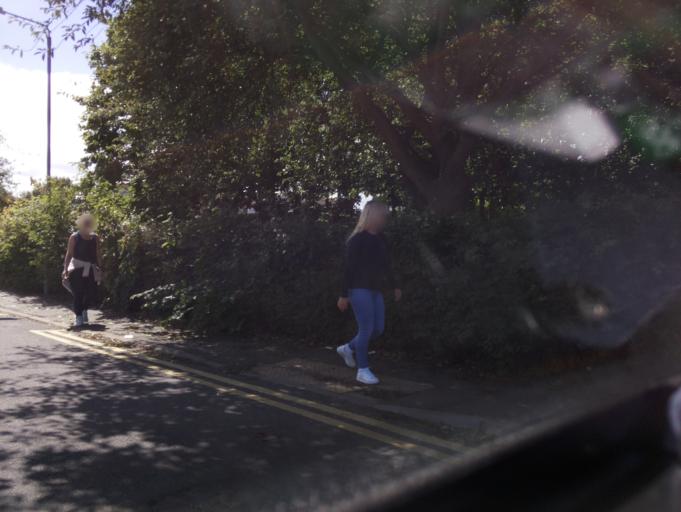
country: GB
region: England
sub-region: Nottinghamshire
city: Cotgrave
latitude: 52.8740
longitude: -1.0830
